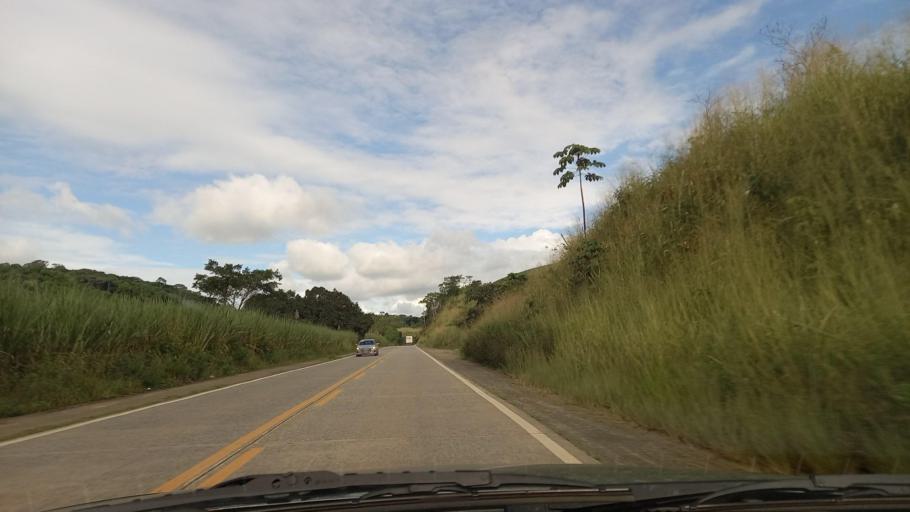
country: BR
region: Pernambuco
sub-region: Catende
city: Catende
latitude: -8.6910
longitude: -35.7020
